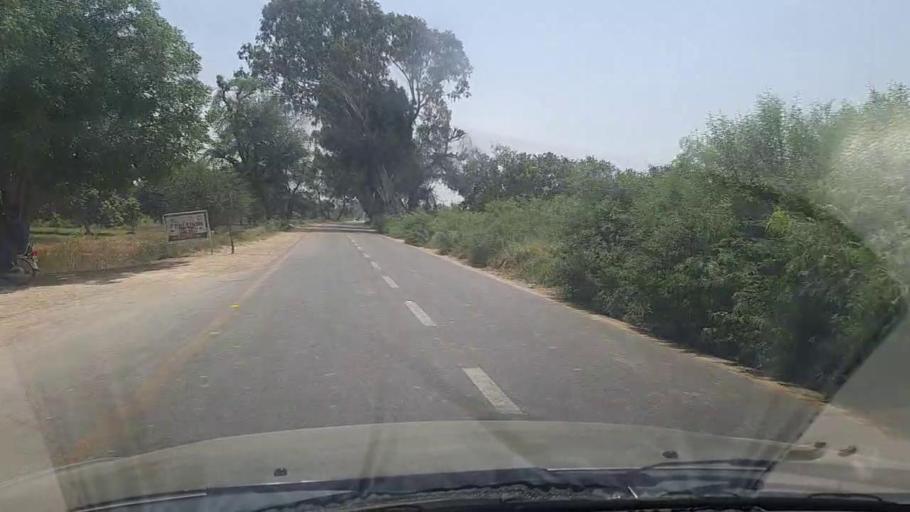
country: PK
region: Sindh
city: Tando Jam
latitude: 25.3271
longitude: 68.5458
